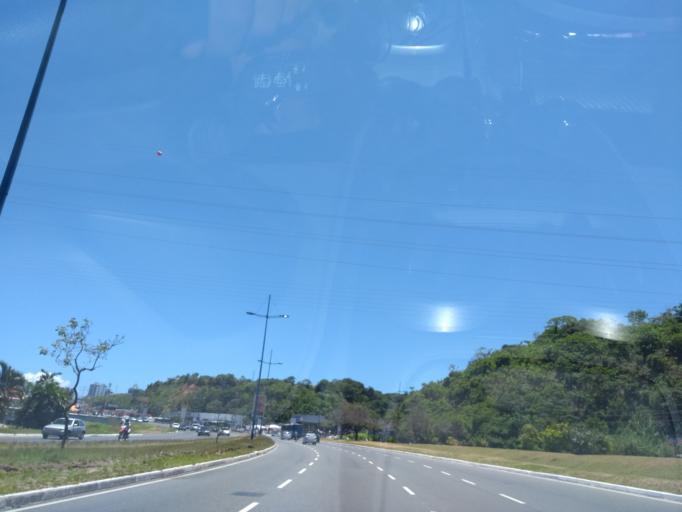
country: BR
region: Bahia
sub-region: Salvador
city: Salvador
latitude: -12.9760
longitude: -38.4764
